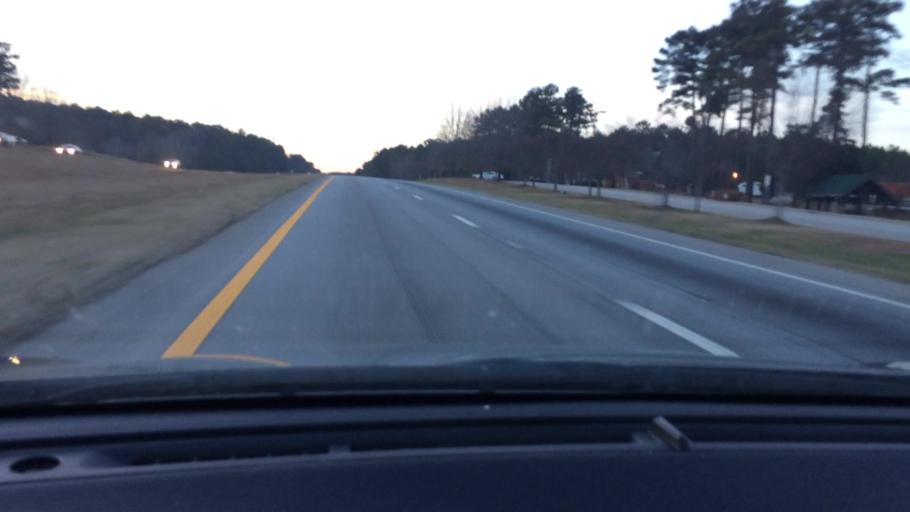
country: US
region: South Carolina
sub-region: Laurens County
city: Joanna
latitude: 34.4120
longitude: -81.7047
